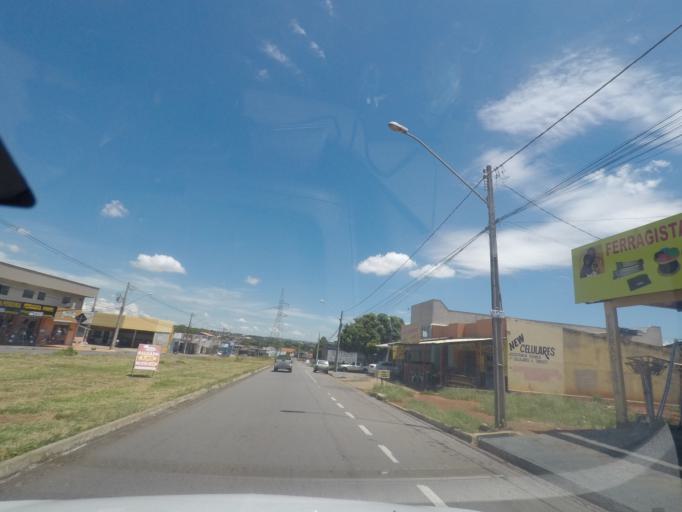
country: BR
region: Goias
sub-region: Goiania
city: Goiania
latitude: -16.7325
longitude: -49.3511
